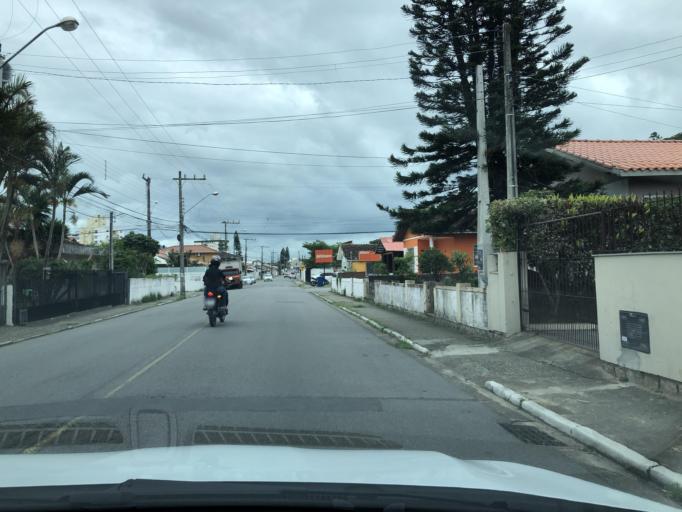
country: BR
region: Santa Catarina
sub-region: Florianopolis
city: Saco dos Limoes
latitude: -27.6052
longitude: -48.5369
